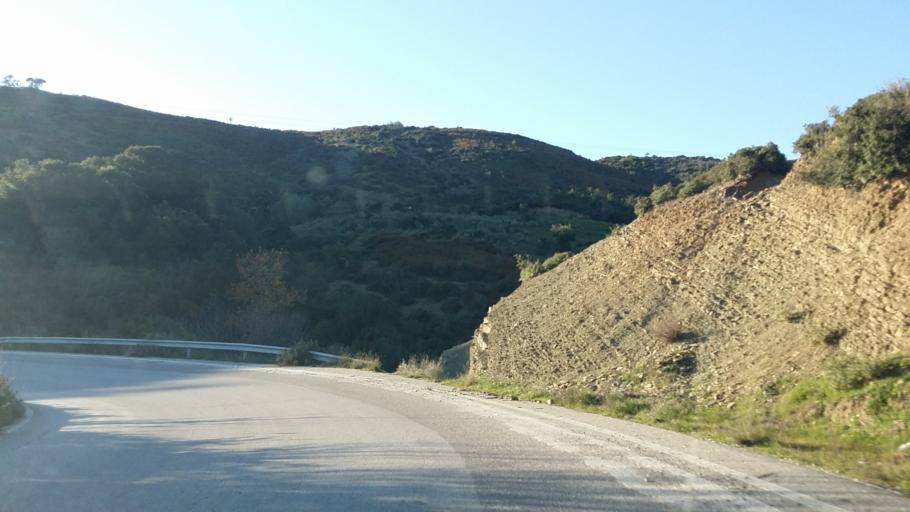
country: GR
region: West Greece
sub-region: Nomos Aitolias kai Akarnanias
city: Lepenou
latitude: 38.8385
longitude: 21.3298
